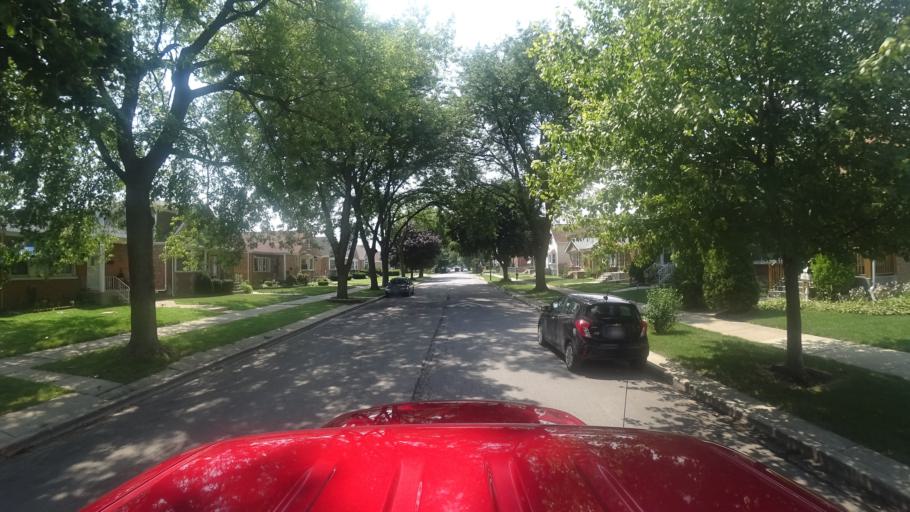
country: US
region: Illinois
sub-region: Cook County
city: Cicero
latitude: 41.7979
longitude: -87.7159
